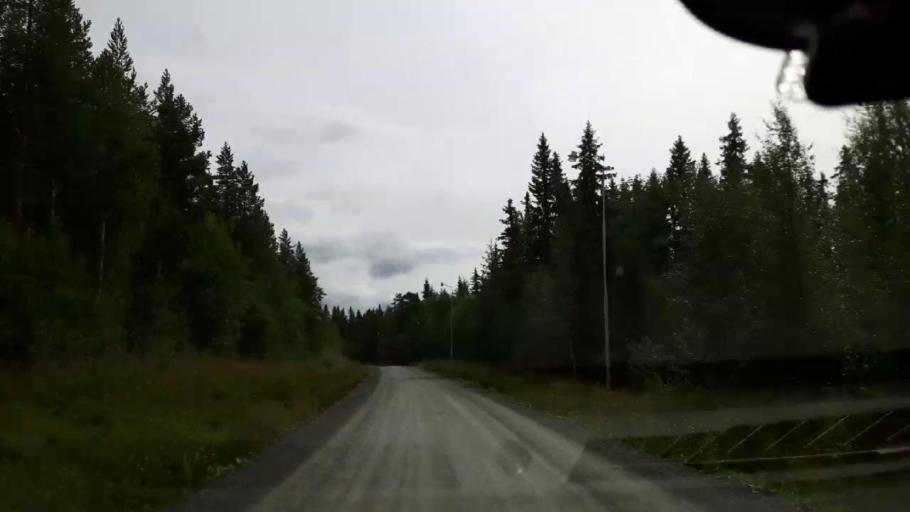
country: SE
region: Jaemtland
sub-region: Krokoms Kommun
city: Valla
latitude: 63.6297
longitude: 14.0206
